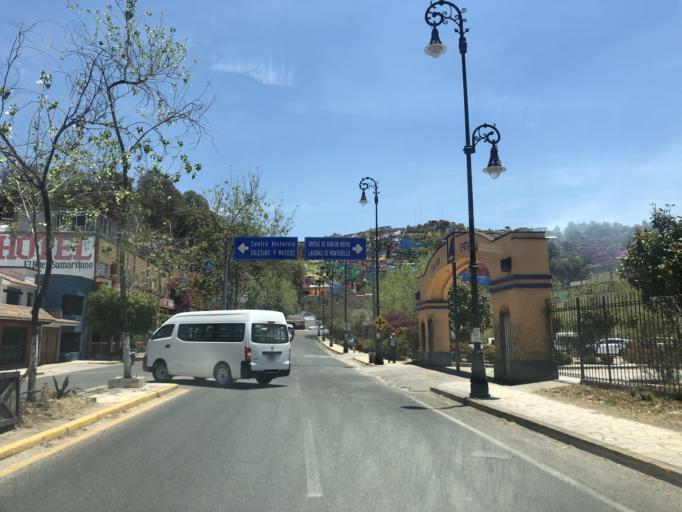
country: MX
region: Chiapas
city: San Cristobal de las Casas
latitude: 16.7212
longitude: -92.6354
